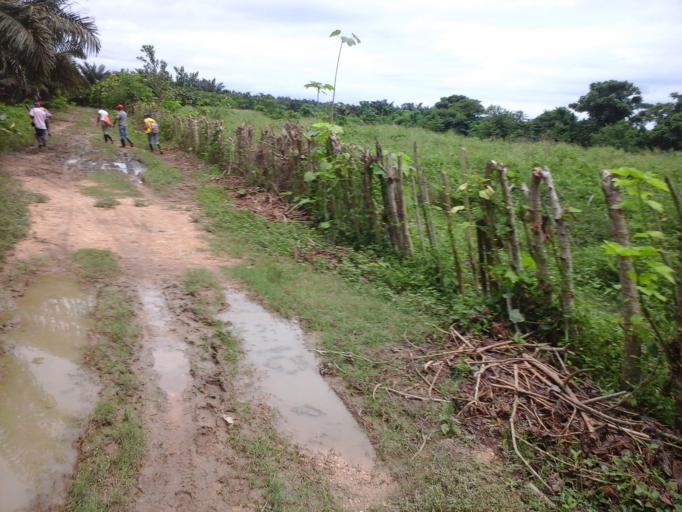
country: CO
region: Bolivar
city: Mahates
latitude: 10.1631
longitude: -75.2763
